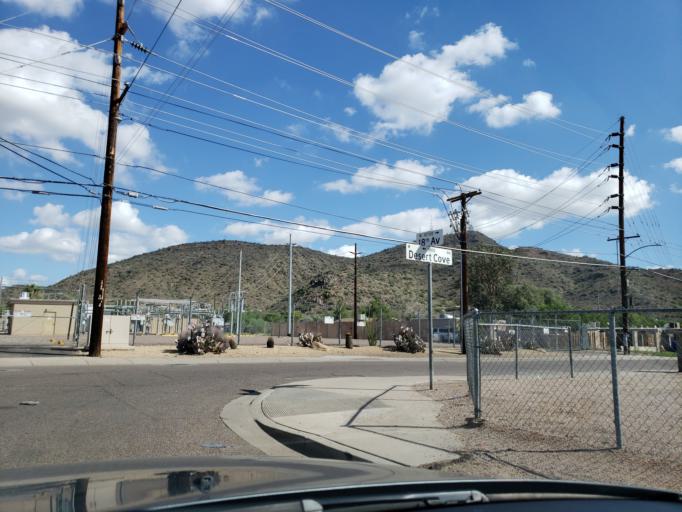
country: US
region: Arizona
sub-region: Maricopa County
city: Glendale
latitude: 33.5856
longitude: -112.0975
